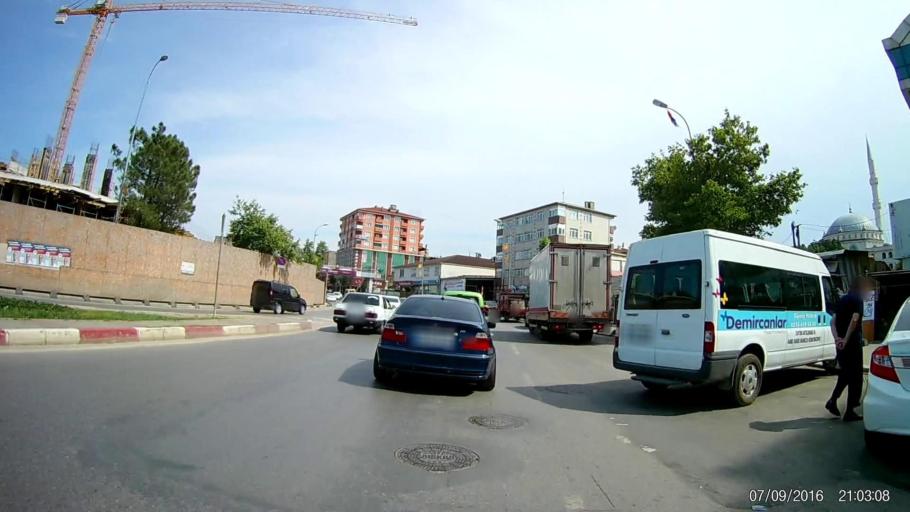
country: TR
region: Istanbul
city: Sultanbeyli
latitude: 40.9695
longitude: 29.2507
